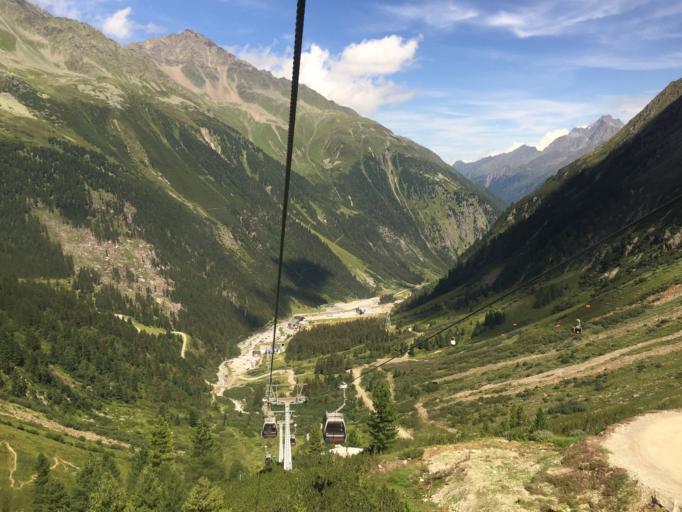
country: AT
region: Tyrol
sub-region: Politischer Bezirk Imst
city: Soelden
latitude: 47.0024
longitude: 11.1463
